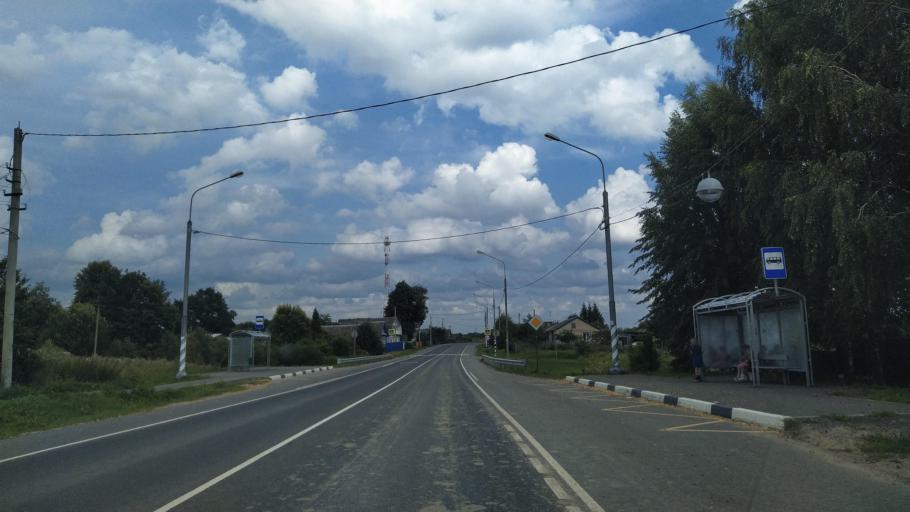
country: RU
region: Pskov
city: Dno
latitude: 58.0623
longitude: 29.9915
